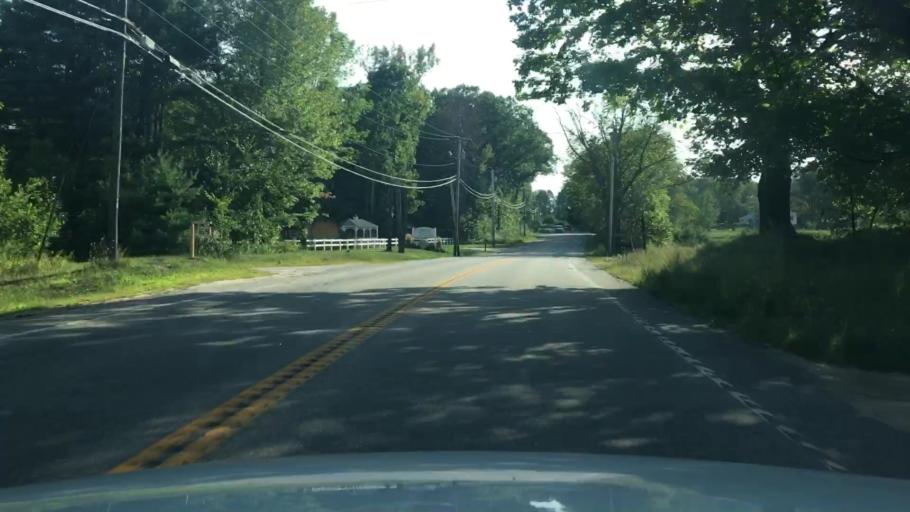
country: US
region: Maine
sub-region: Cumberland County
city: New Gloucester
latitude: 43.9148
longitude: -70.3200
